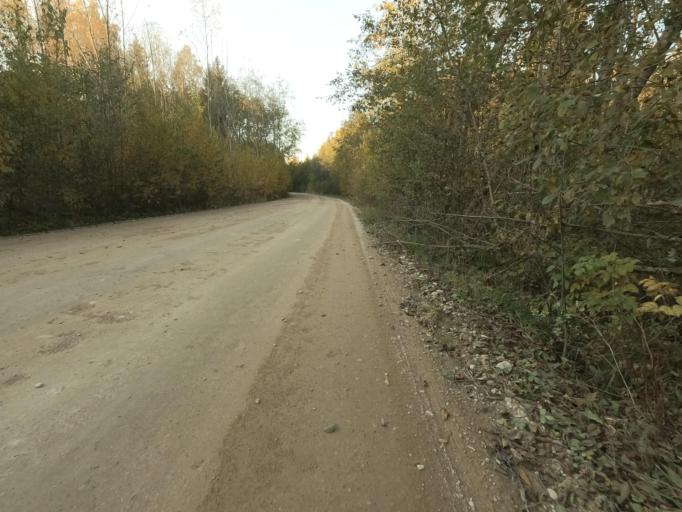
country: RU
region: Leningrad
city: Lyuban'
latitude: 58.9956
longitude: 31.1058
